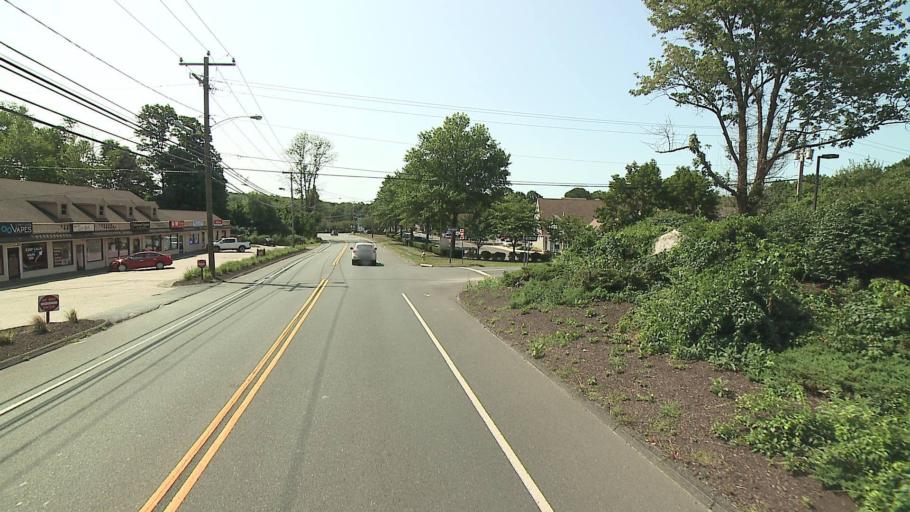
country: US
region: Connecticut
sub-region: Fairfield County
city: Newtown
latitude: 41.3263
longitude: -73.2671
